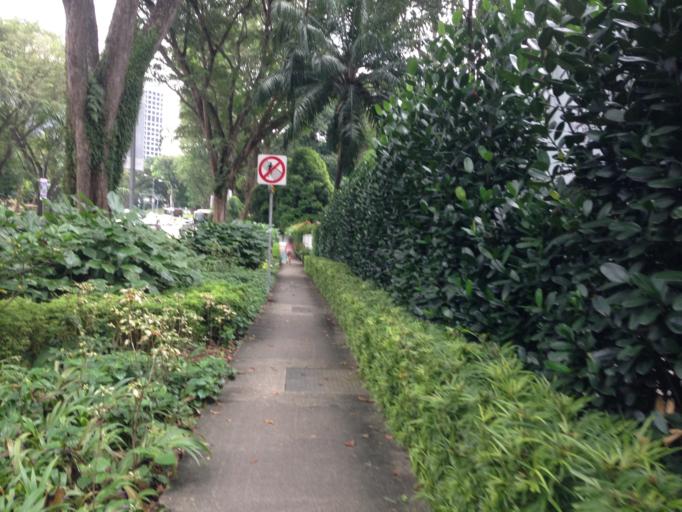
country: SG
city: Singapore
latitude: 1.3106
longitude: 103.8351
